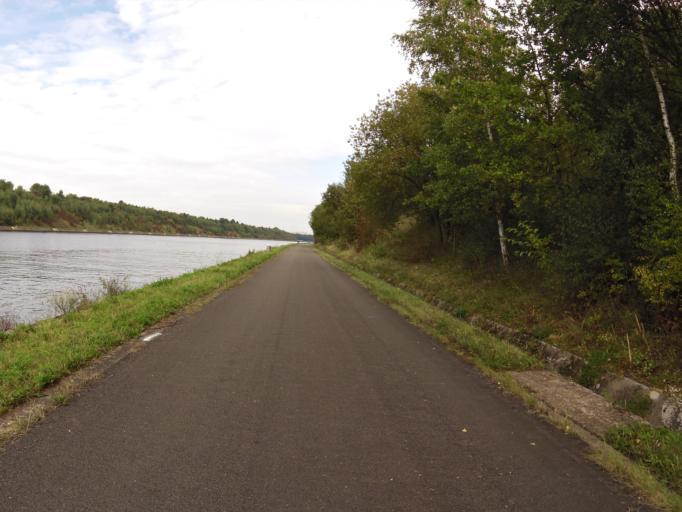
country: BE
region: Flanders
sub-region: Provincie Limburg
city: Lanaken
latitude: 50.8634
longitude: 5.6398
